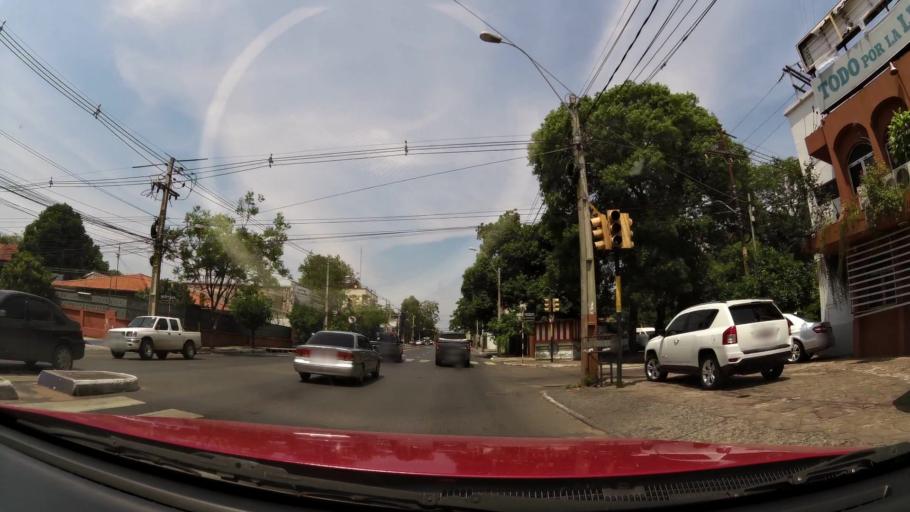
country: PY
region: Asuncion
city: Asuncion
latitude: -25.3001
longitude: -57.5939
